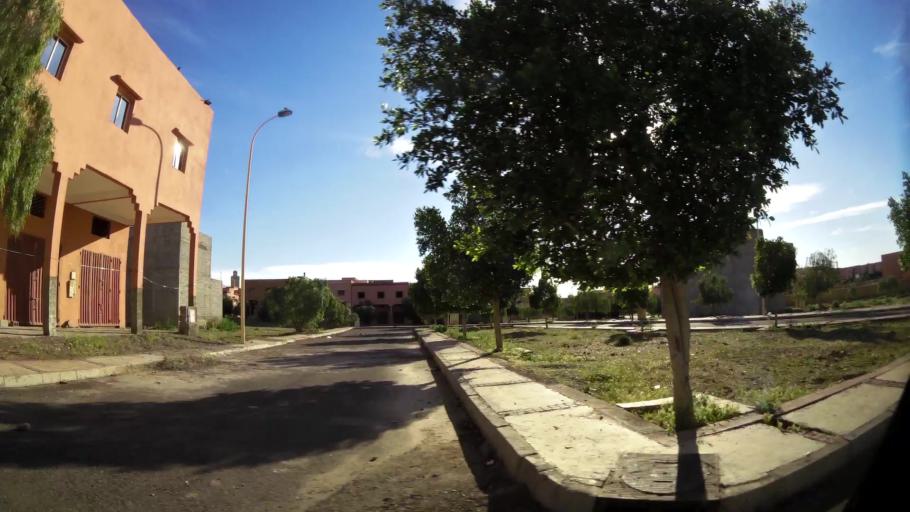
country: MA
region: Marrakech-Tensift-Al Haouz
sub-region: Marrakech
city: Marrakesh
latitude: 31.7604
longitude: -8.0964
